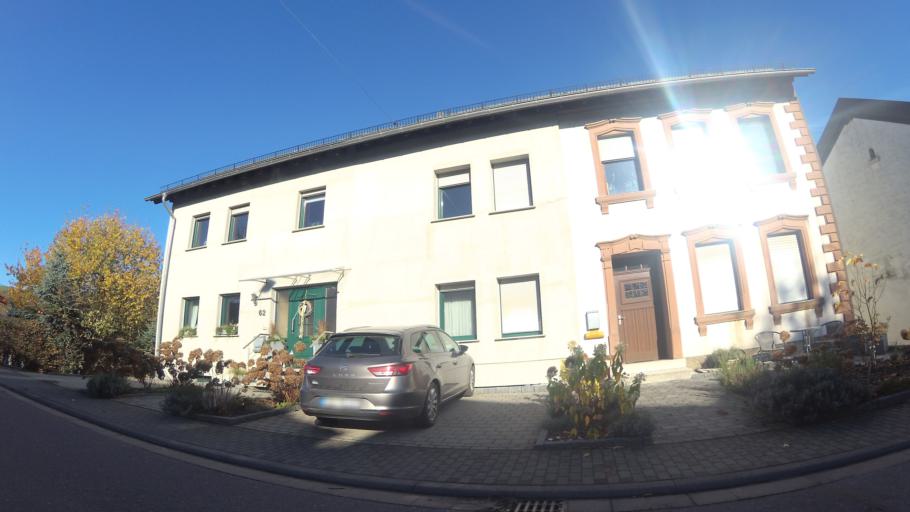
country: DE
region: Saarland
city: Losheim
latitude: 49.4875
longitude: 6.7726
